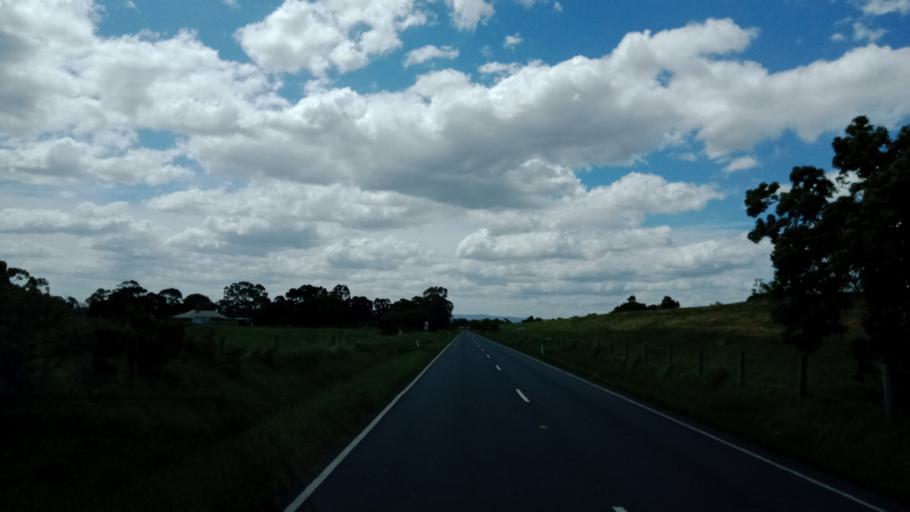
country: AU
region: Victoria
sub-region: Kingston
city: Chelsea Heights
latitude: -38.0403
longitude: 145.1765
